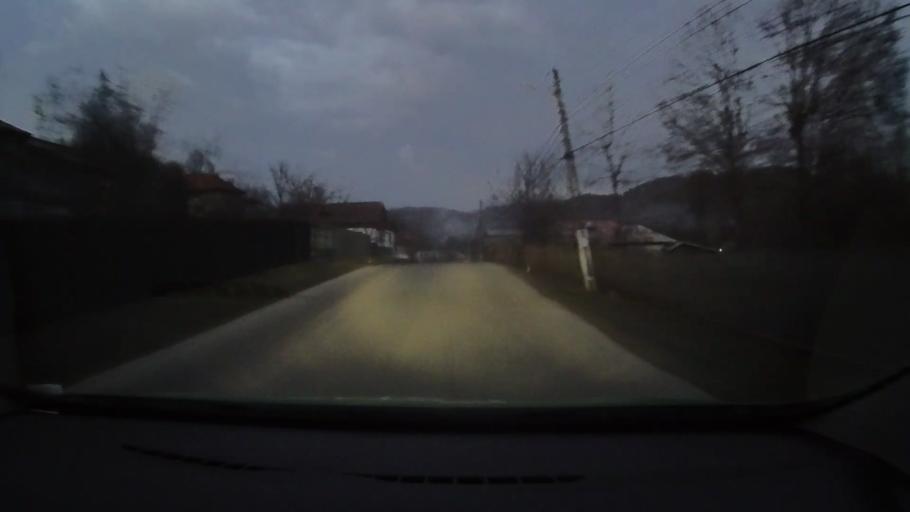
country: RO
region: Prahova
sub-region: Comuna Poiana Campina
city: Poiana Campina
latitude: 45.1206
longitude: 25.6703
